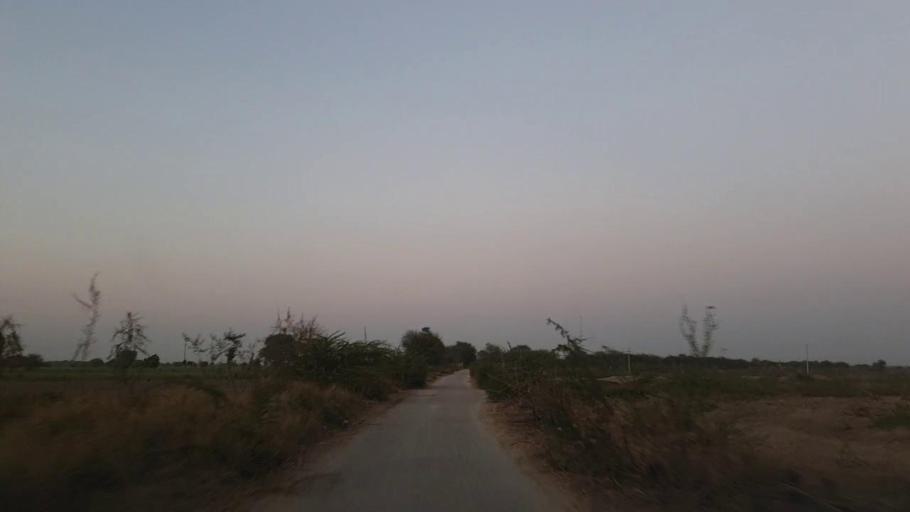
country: PK
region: Sindh
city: Naukot
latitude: 24.8727
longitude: 69.3853
